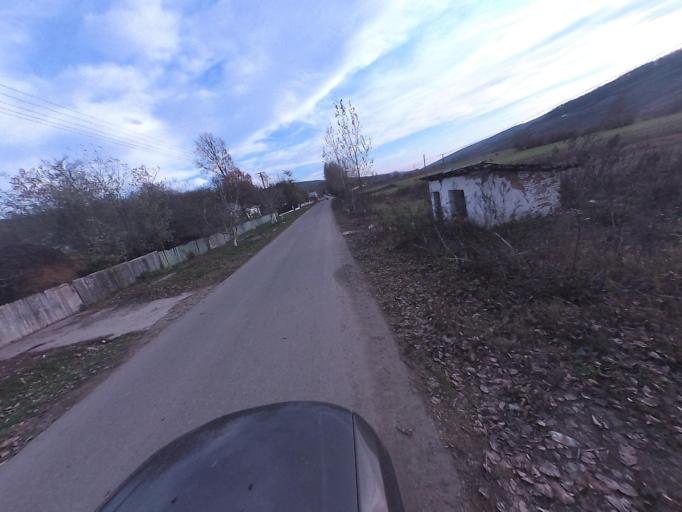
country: RO
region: Vaslui
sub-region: Comuna Gherghesti
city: Gherghesti
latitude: 46.4901
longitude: 27.5337
